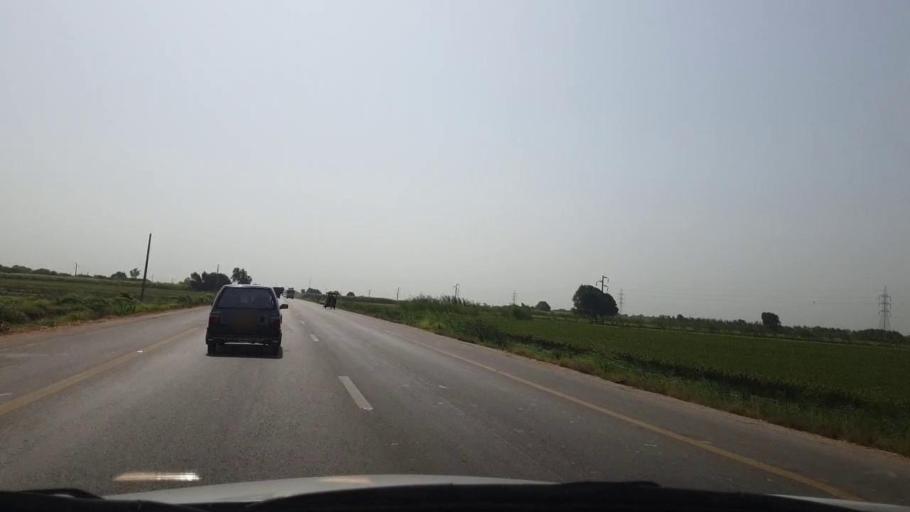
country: PK
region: Sindh
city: Tando Muhammad Khan
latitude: 25.1129
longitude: 68.5782
